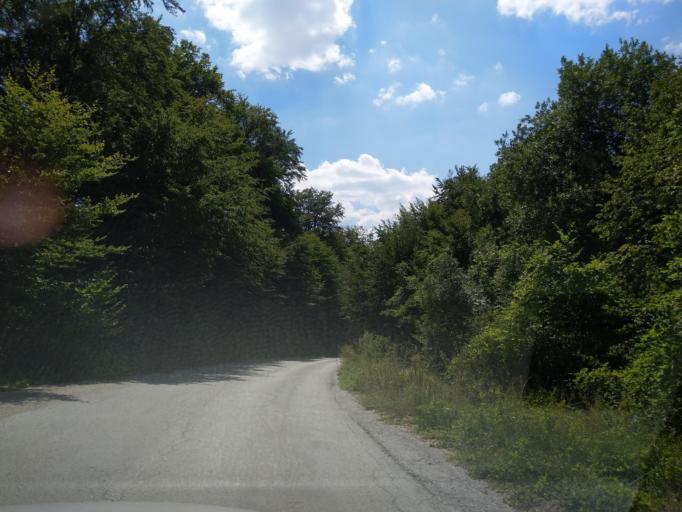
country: RS
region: Central Serbia
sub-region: Zlatiborski Okrug
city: Nova Varos
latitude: 43.4277
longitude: 19.9383
